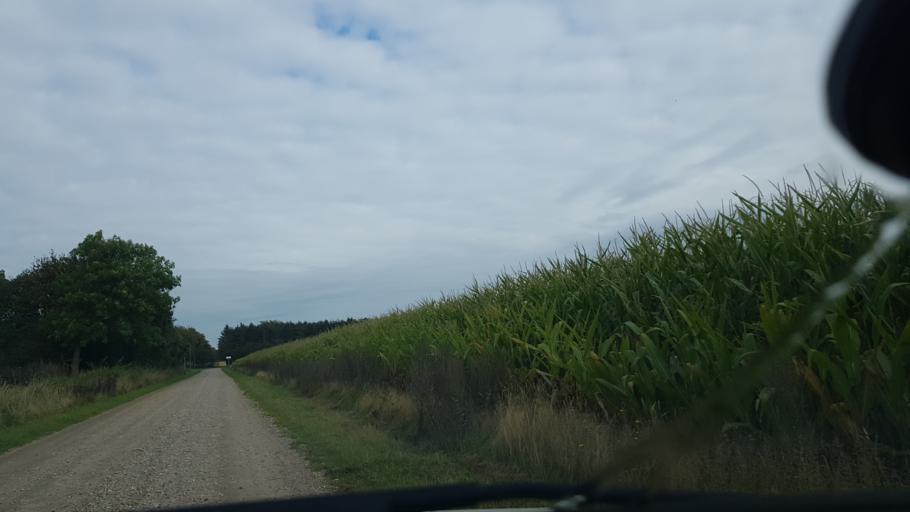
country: DK
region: South Denmark
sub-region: Vejen Kommune
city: Holsted
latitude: 55.4469
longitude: 8.9317
